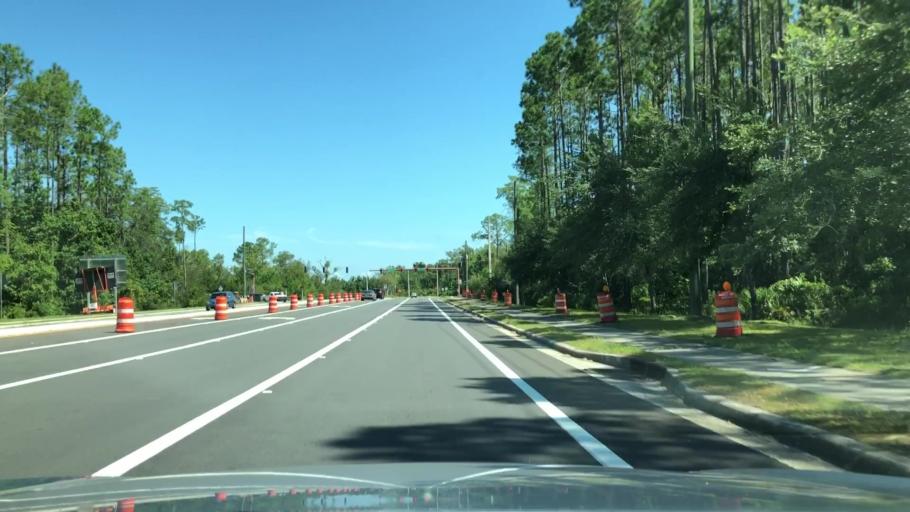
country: US
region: Florida
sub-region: Saint Johns County
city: Fruit Cove
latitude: 30.0834
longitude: -81.5321
